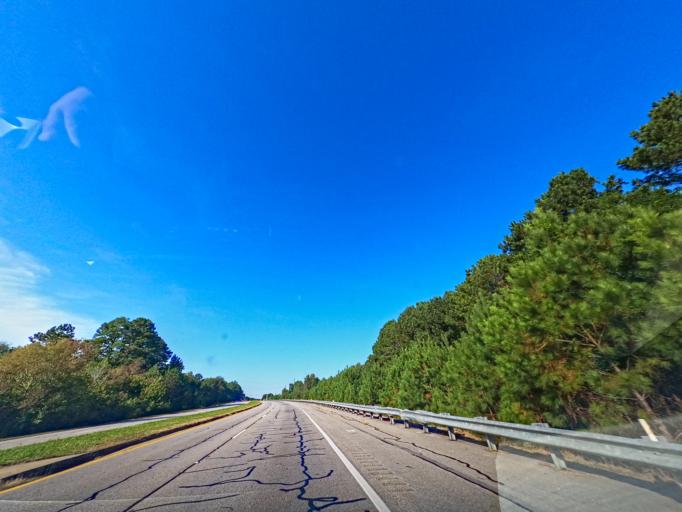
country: US
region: Georgia
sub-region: Coweta County
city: Newnan
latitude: 33.3976
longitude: -84.8208
